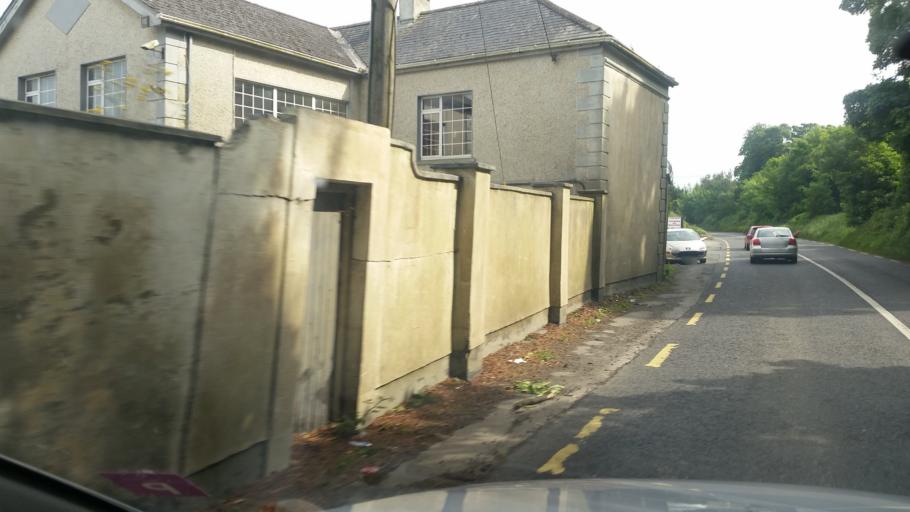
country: IE
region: Leinster
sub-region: Dublin City
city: Finglas
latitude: 53.4168
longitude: -6.3072
